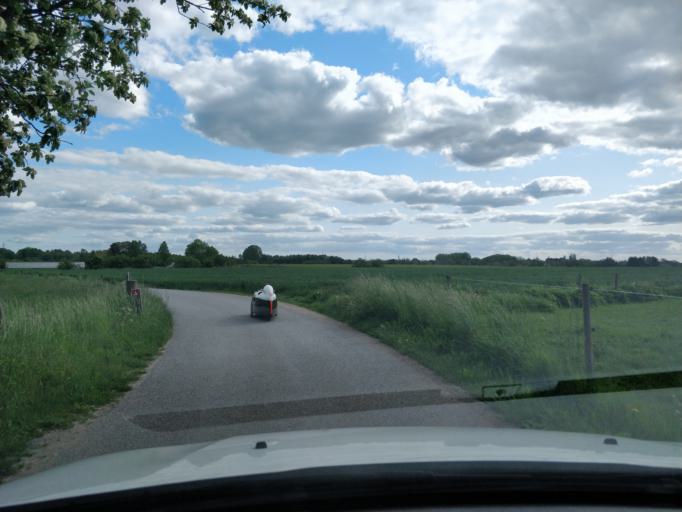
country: DK
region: Capital Region
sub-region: Hoje-Taastrup Kommune
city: Flong
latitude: 55.6870
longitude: 12.2184
